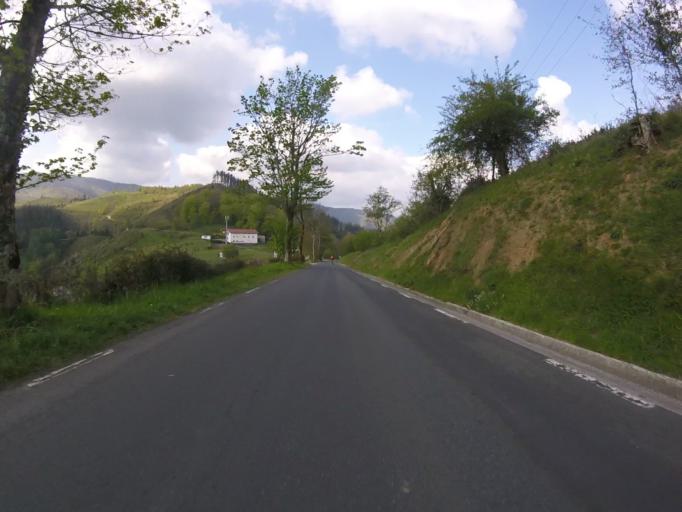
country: ES
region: Basque Country
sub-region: Provincia de Guipuzcoa
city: Elgoibar
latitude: 43.2041
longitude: -2.3600
